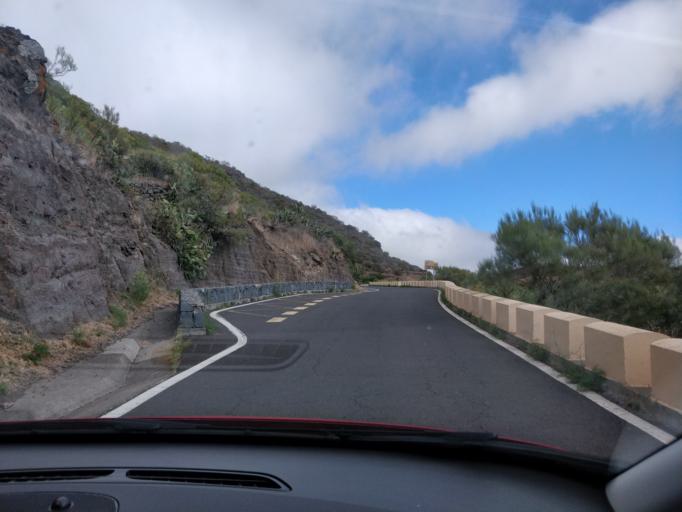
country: ES
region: Canary Islands
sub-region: Provincia de Santa Cruz de Tenerife
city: Santiago del Teide
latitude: 28.3148
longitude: -16.8472
